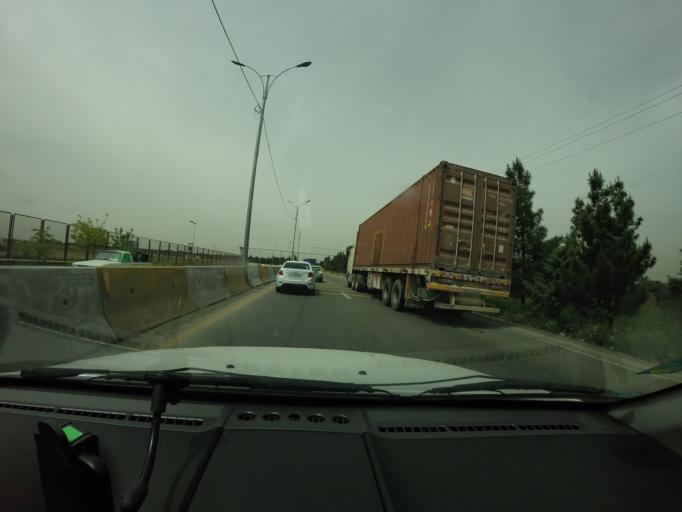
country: IR
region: Tehran
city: Eslamshahr
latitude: 35.5944
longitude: 51.2435
